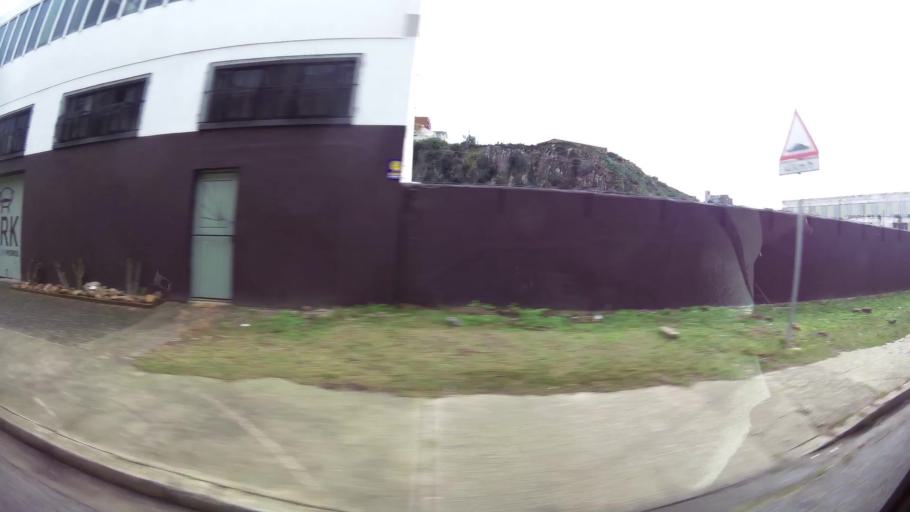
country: ZA
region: Eastern Cape
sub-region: Nelson Mandela Bay Metropolitan Municipality
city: Port Elizabeth
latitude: -33.9686
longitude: 25.6216
